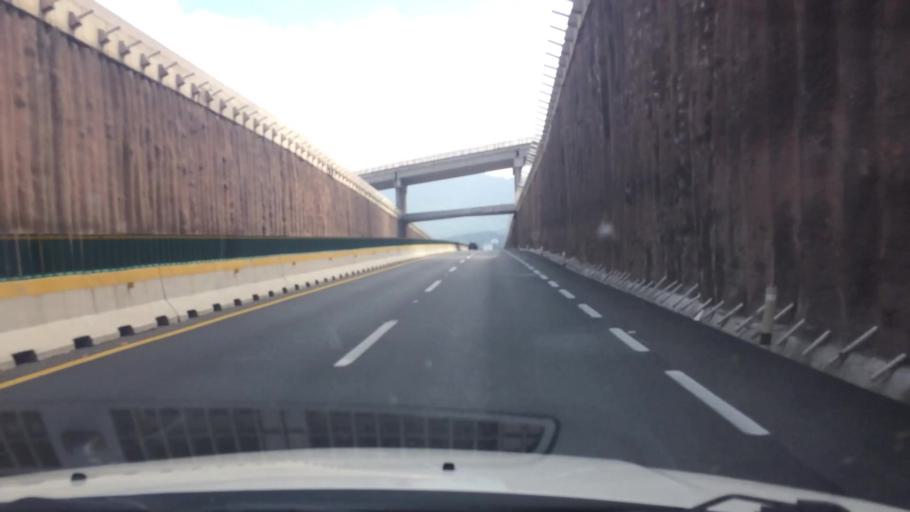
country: MX
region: Morelos
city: San Jeronimo Acazulco
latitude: 19.2987
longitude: -99.3935
